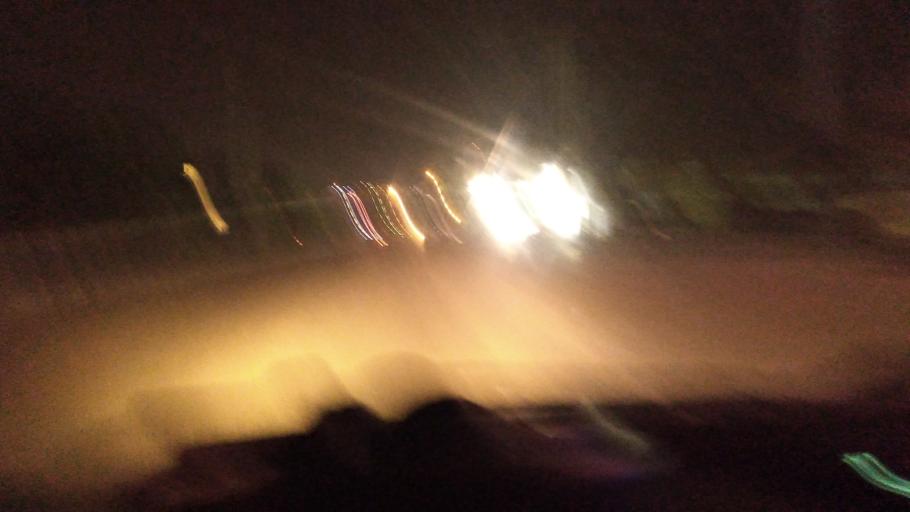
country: IR
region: Khuzestan
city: Ahvaz
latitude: 31.3070
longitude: 48.7541
